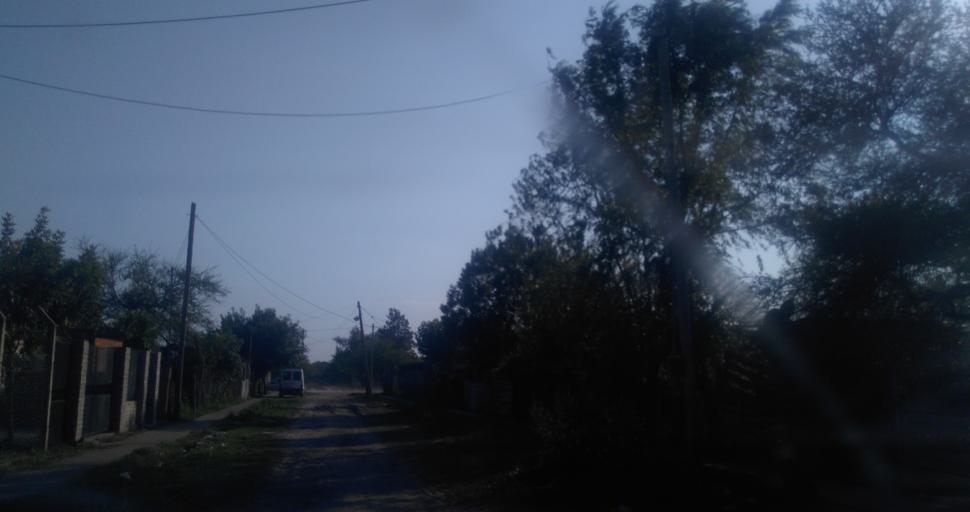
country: AR
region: Chaco
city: Resistencia
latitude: -27.4825
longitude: -59.0064
